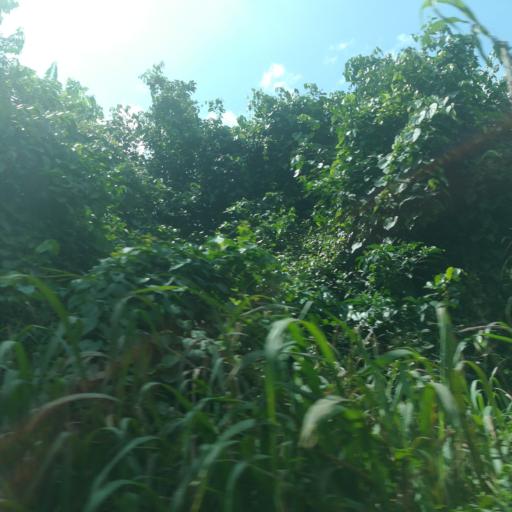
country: NG
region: Lagos
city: Ikorodu
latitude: 6.6646
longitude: 3.6370
